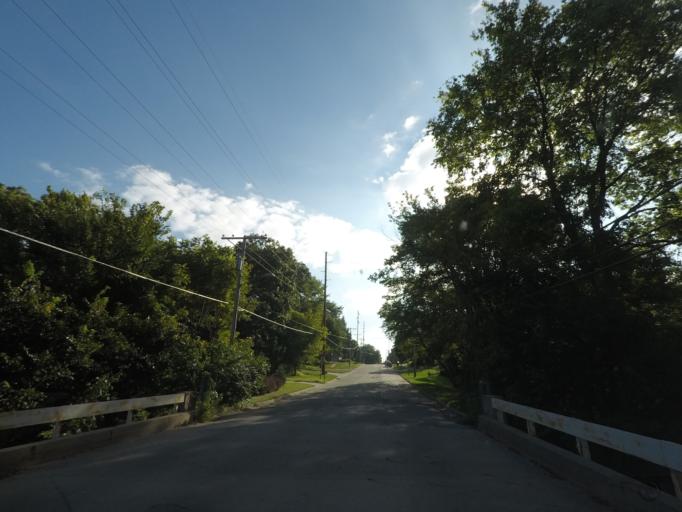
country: US
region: Iowa
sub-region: Story County
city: Nevada
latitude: 42.0156
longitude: -93.4564
